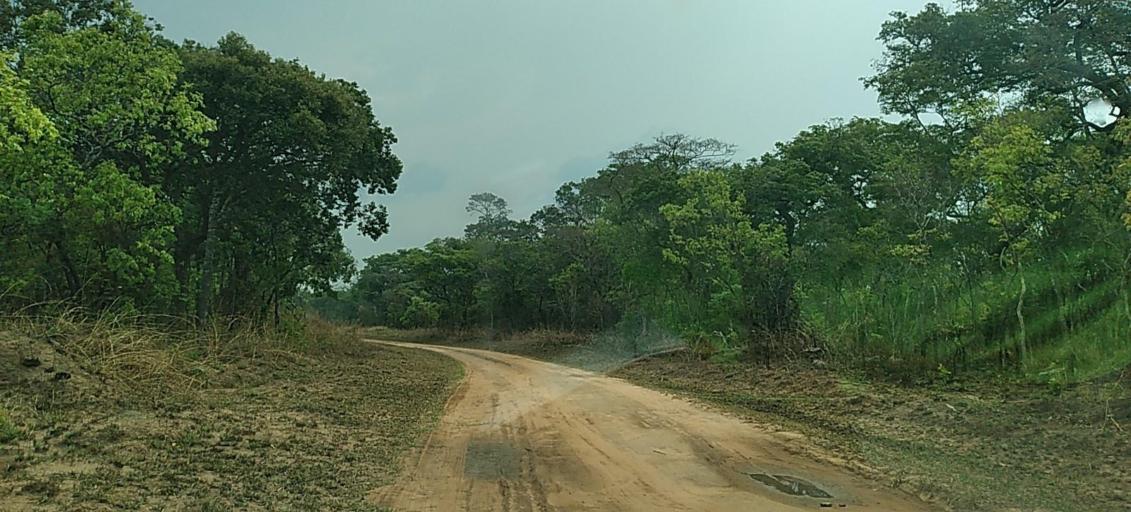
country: ZM
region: North-Western
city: Mwinilunga
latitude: -11.4668
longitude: 24.4700
